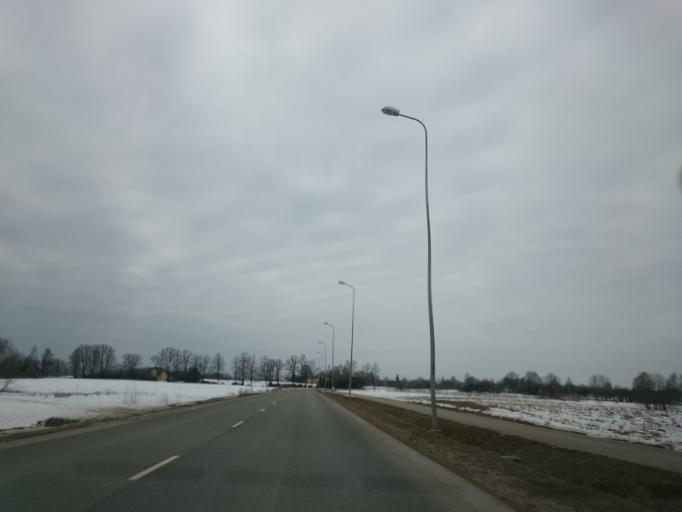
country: LV
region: Cesu Rajons
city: Cesis
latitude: 57.2966
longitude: 25.2535
